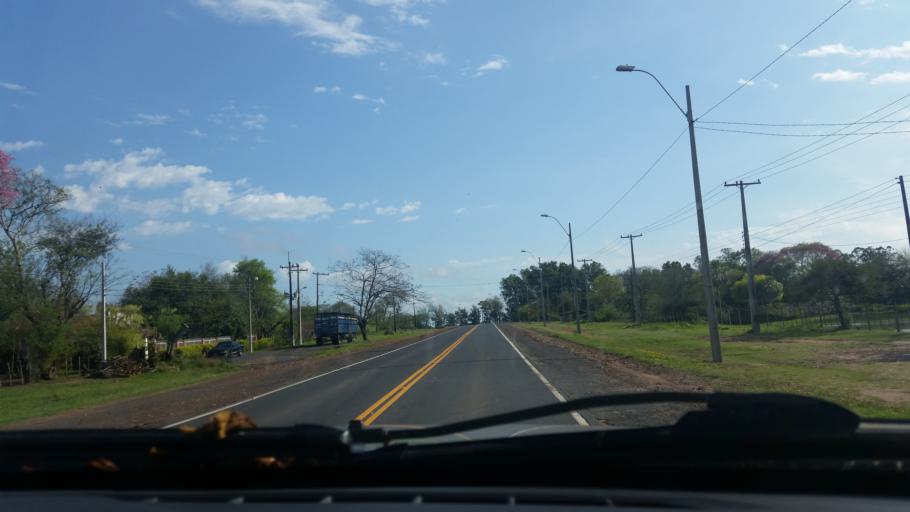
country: PY
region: Presidente Hayes
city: Villa Hayes
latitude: -25.0633
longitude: -57.5340
